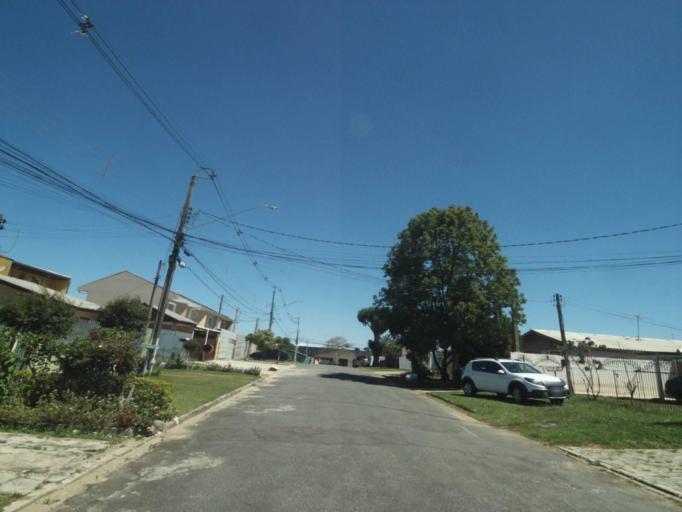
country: BR
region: Parana
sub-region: Curitiba
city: Curitiba
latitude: -25.4793
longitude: -49.3448
